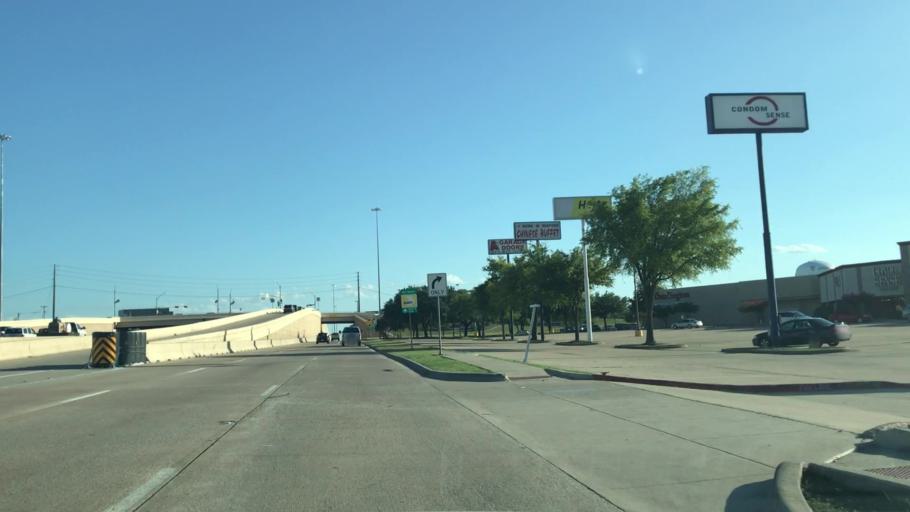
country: US
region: Texas
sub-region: Collin County
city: Plano
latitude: 33.0402
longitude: -96.7035
